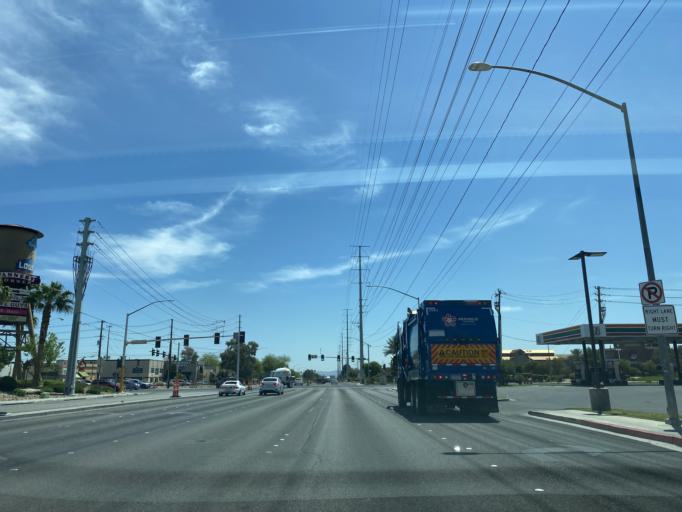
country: US
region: Nevada
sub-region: Clark County
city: North Las Vegas
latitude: 36.2408
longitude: -115.1169
